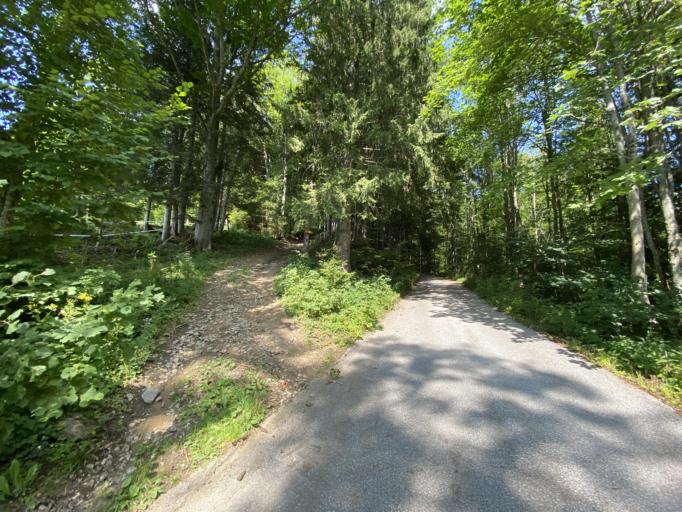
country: AT
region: Lower Austria
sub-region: Politischer Bezirk Lilienfeld
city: Annaberg
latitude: 47.8785
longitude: 15.3616
